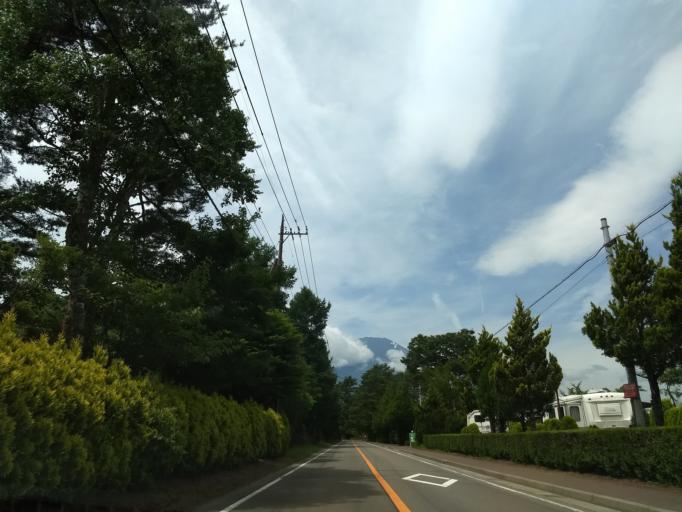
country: JP
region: Shizuoka
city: Gotemba
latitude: 35.4142
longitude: 138.8947
